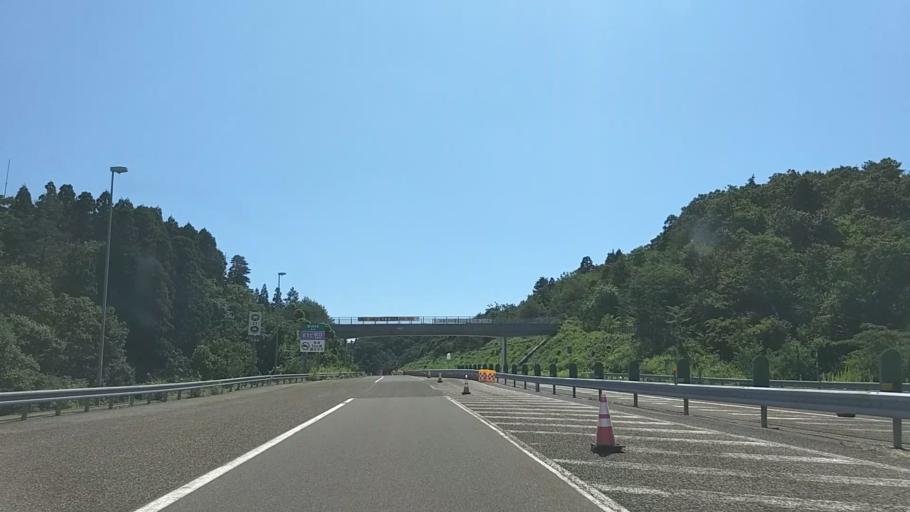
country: JP
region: Niigata
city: Joetsu
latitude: 37.1259
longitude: 138.2128
